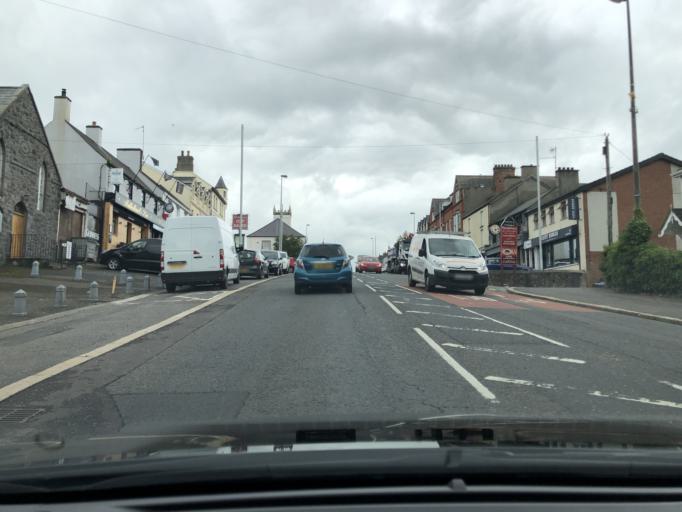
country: GB
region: Northern Ireland
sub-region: Down District
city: Castlewellan
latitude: 54.2584
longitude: -5.9402
